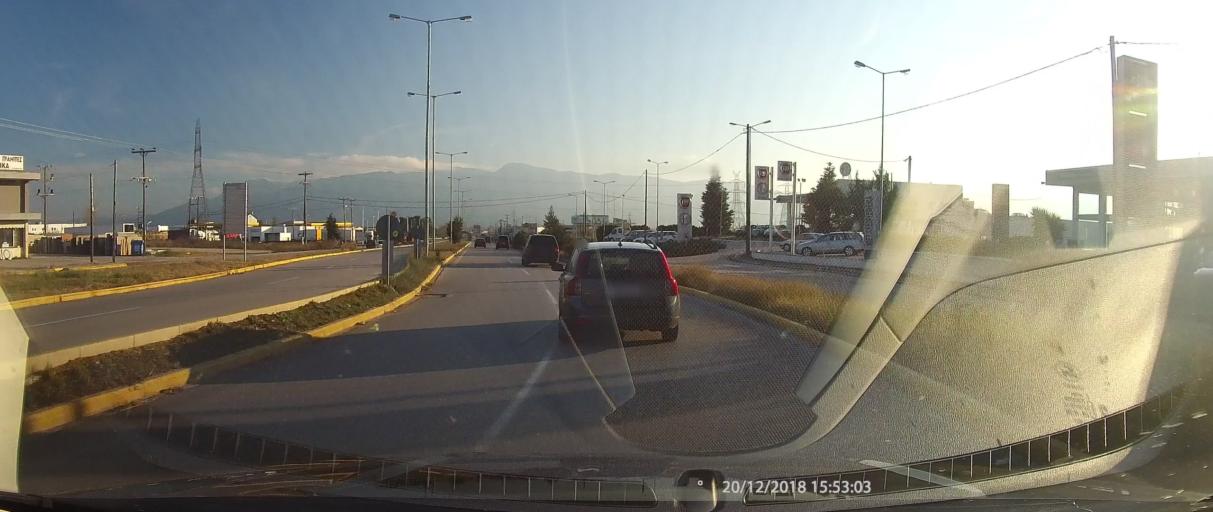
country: GR
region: Central Greece
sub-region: Nomos Fthiotidos
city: Rodhitsa
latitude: 38.8764
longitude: 22.4539
